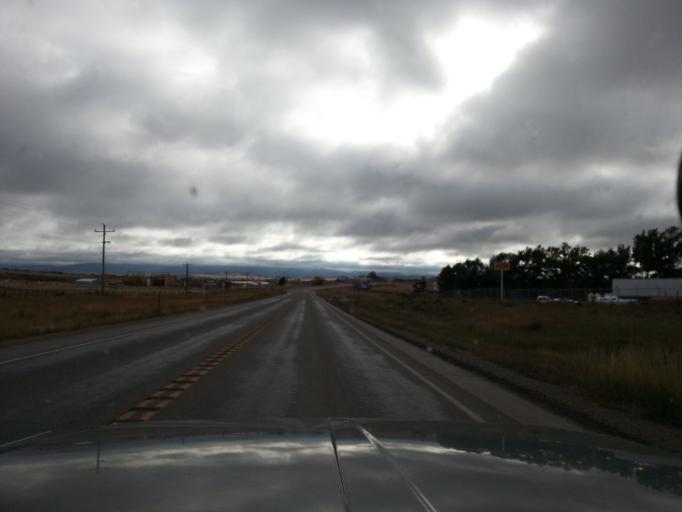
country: US
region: Wyoming
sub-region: Converse County
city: Douglas
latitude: 42.7854
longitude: -105.3690
